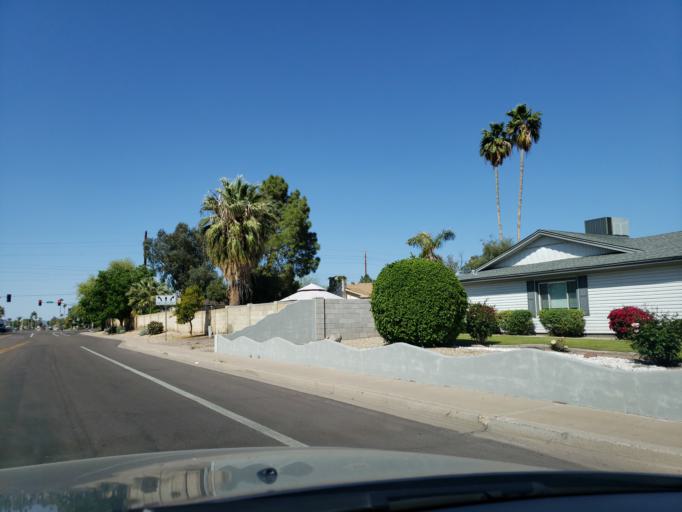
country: US
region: Arizona
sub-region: Maricopa County
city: Glendale
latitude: 33.5664
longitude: -112.1776
